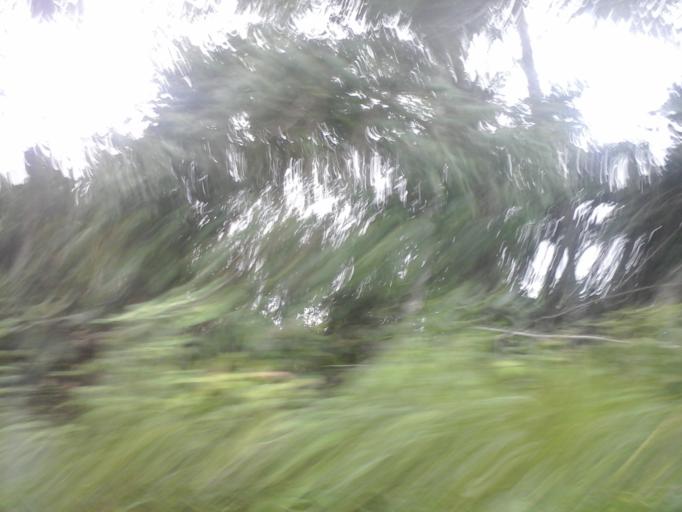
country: CO
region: Caqueta
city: El Doncello
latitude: 1.6291
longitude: -75.1304
